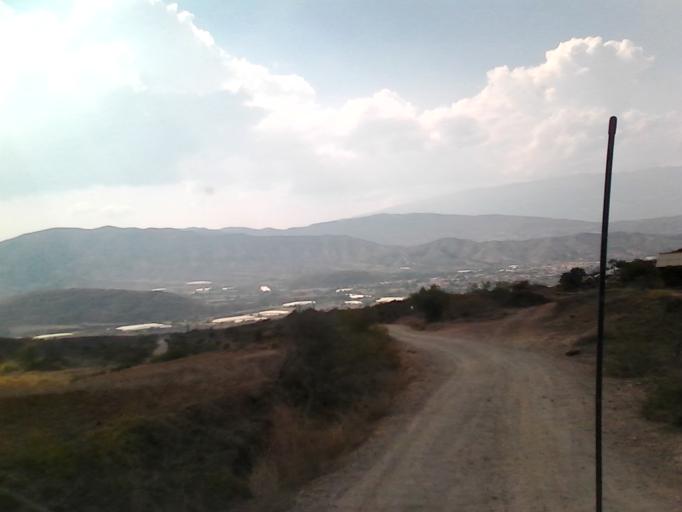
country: CO
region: Boyaca
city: Sachica
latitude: 5.5745
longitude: -73.5210
